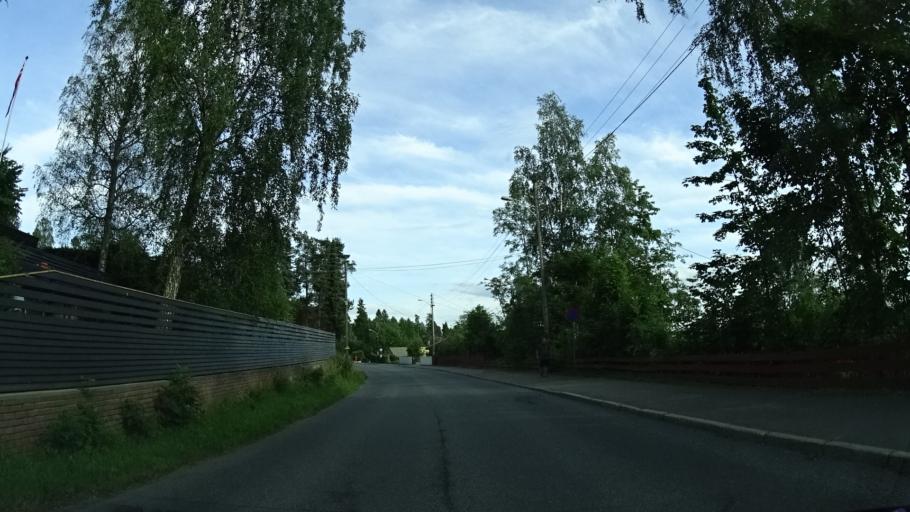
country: NO
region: Oslo
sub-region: Oslo
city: Sjolyststranda
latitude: 59.9612
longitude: 10.6479
